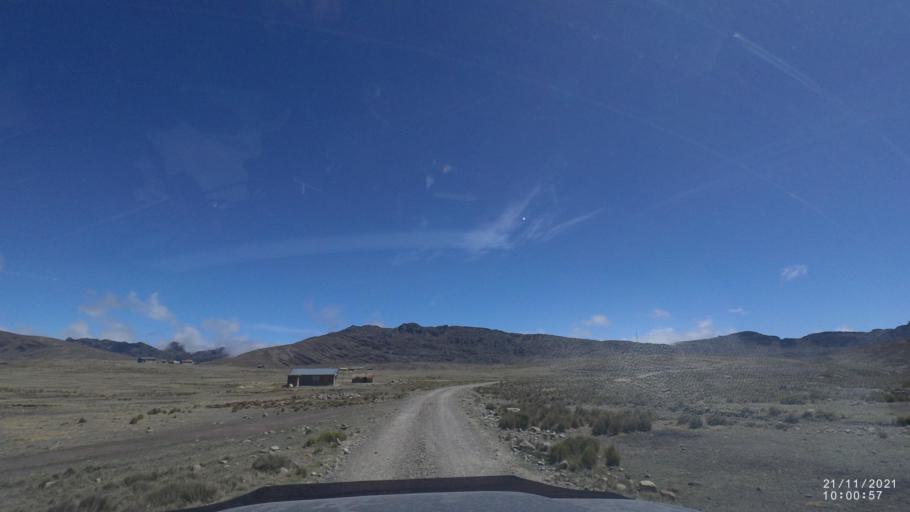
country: BO
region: Cochabamba
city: Cochabamba
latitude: -17.0333
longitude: -66.2791
